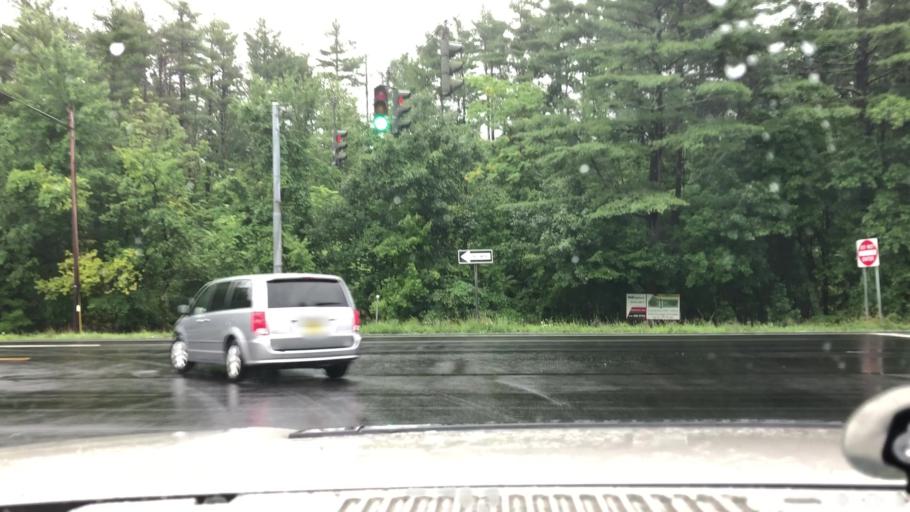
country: US
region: New York
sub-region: Greene County
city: Cairo
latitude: 42.2966
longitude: -73.9889
